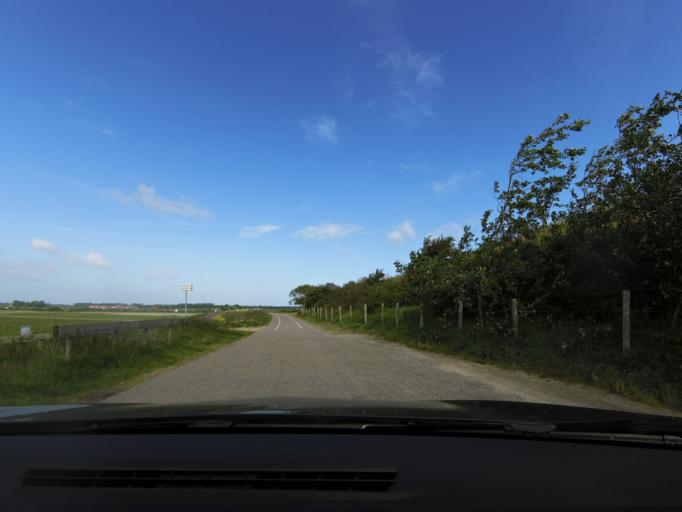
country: NL
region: Zeeland
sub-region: Schouwen-Duiveland
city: Scharendijke
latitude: 51.7391
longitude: 3.8149
